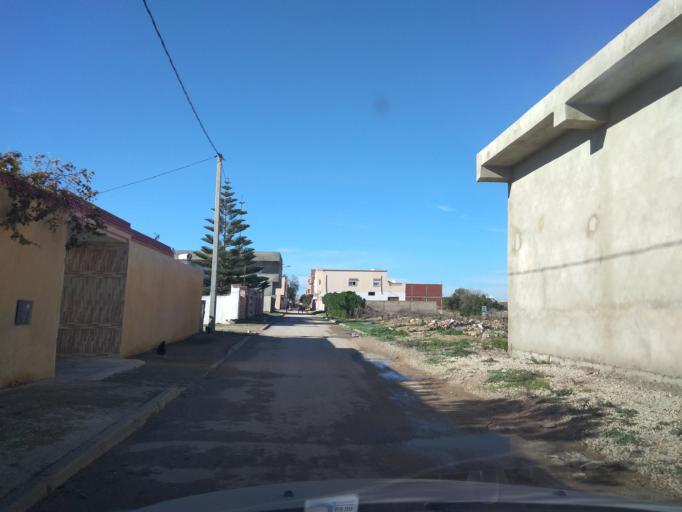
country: TN
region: Ariana
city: Qal'at al Andalus
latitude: 37.0638
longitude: 10.1249
